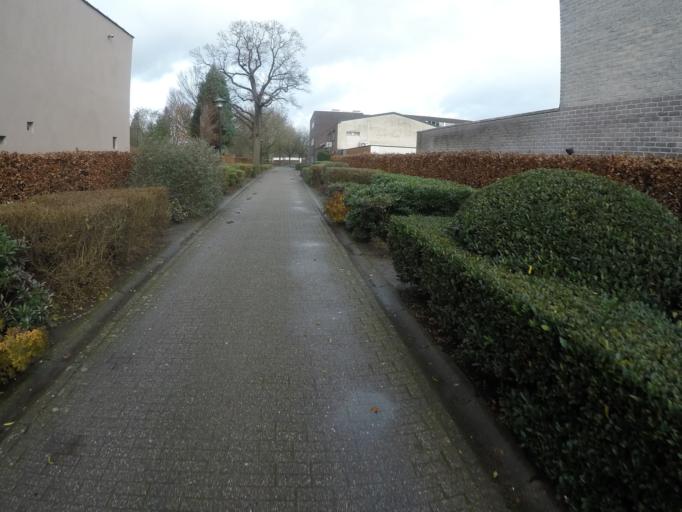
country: BE
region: Flanders
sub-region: Provincie Antwerpen
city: Borsbeek
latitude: 51.1962
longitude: 4.4860
